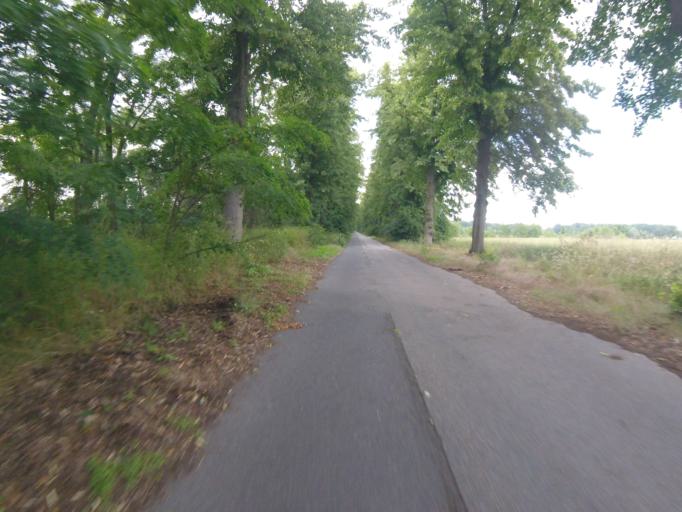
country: DE
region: Brandenburg
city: Konigs Wusterhausen
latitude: 52.3085
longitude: 13.5946
